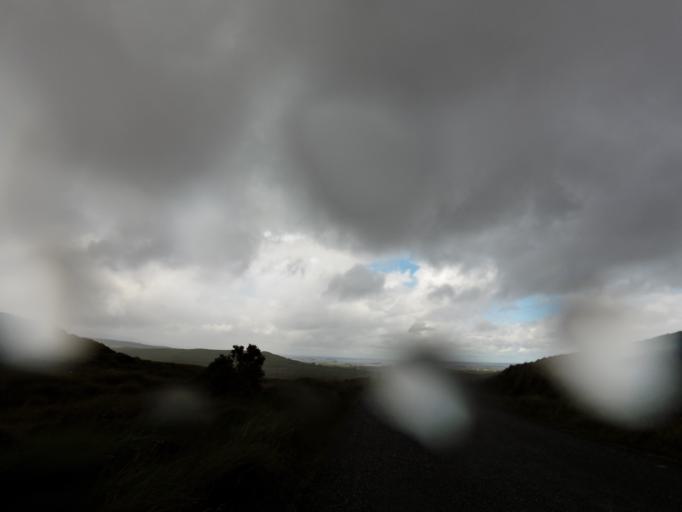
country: IE
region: Connaught
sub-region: County Galway
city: Oughterard
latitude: 53.3951
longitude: -9.3375
